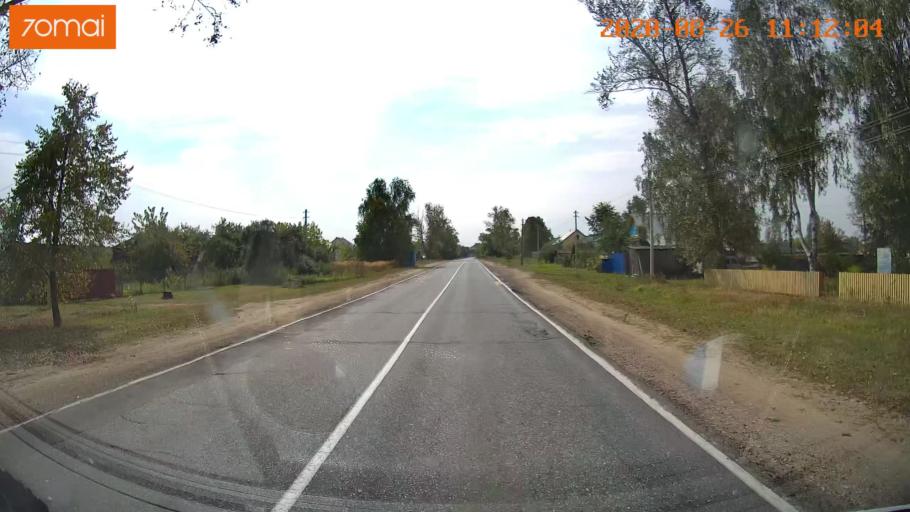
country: RU
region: Rjazan
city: Izhevskoye
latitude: 54.4741
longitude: 41.1257
